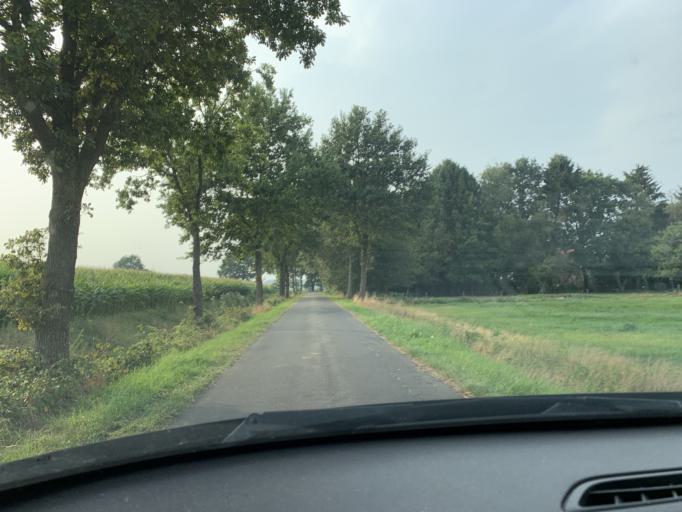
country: DE
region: Lower Saxony
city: Apen
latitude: 53.2434
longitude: 7.8282
